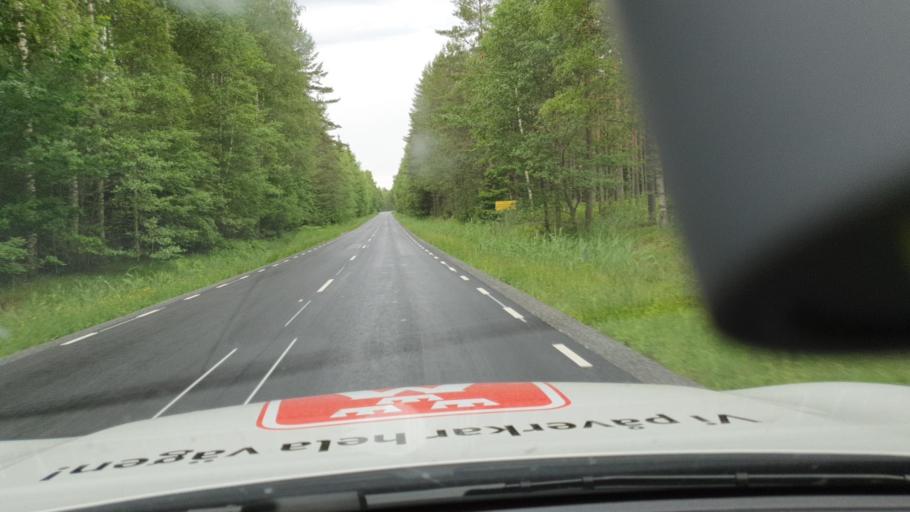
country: SE
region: Vaestra Goetaland
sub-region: Gullspangs Kommun
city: Anderstorp
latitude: 58.9221
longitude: 14.4301
